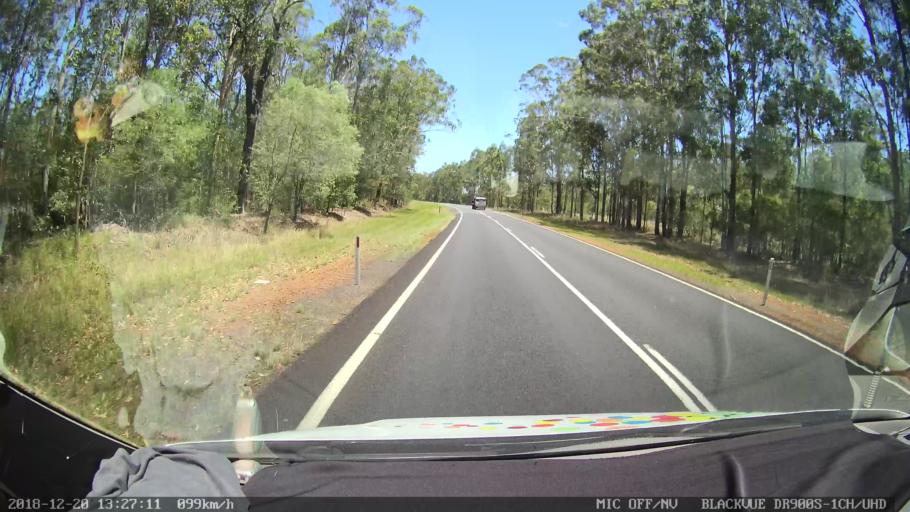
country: AU
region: New South Wales
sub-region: Richmond Valley
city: Casino
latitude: -29.1564
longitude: 152.9924
